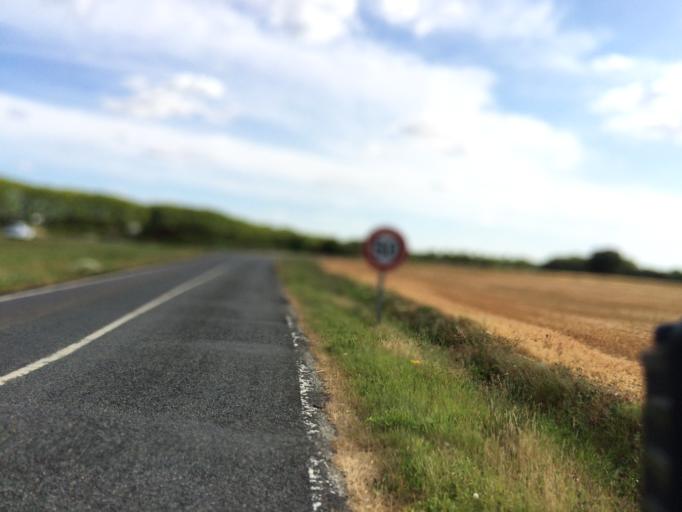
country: FR
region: Ile-de-France
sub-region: Departement de l'Essonne
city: Tigery
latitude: 48.6388
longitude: 2.5007
